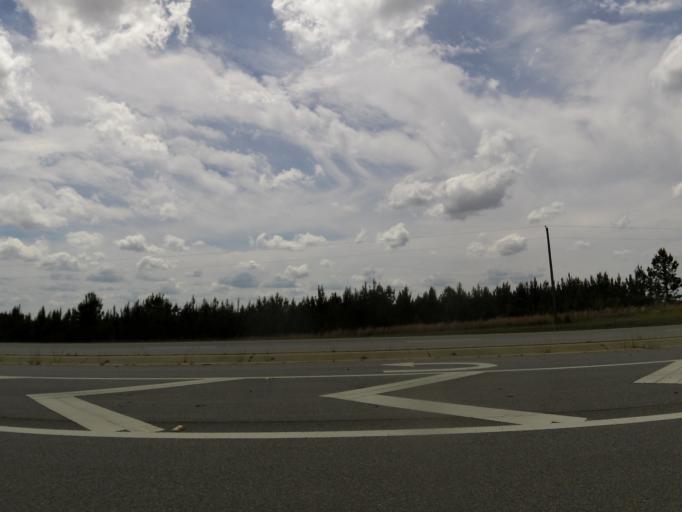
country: US
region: Georgia
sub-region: Jefferson County
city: Wadley
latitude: 32.7253
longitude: -82.3950
